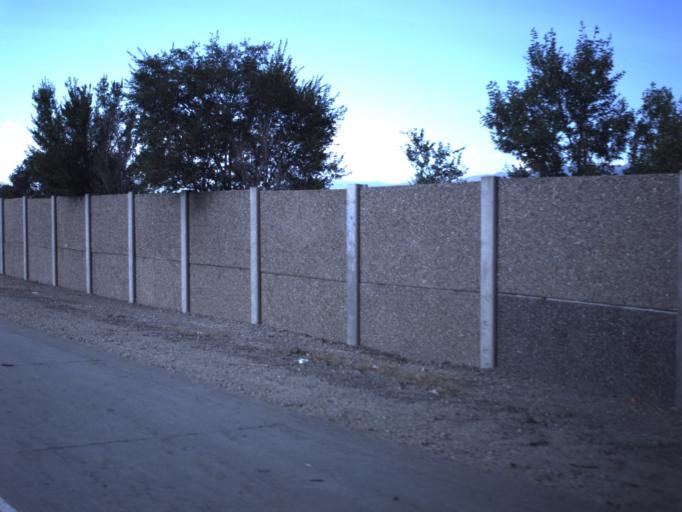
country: US
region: Utah
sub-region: Salt Lake County
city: Taylorsville
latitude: 40.6510
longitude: -111.9518
